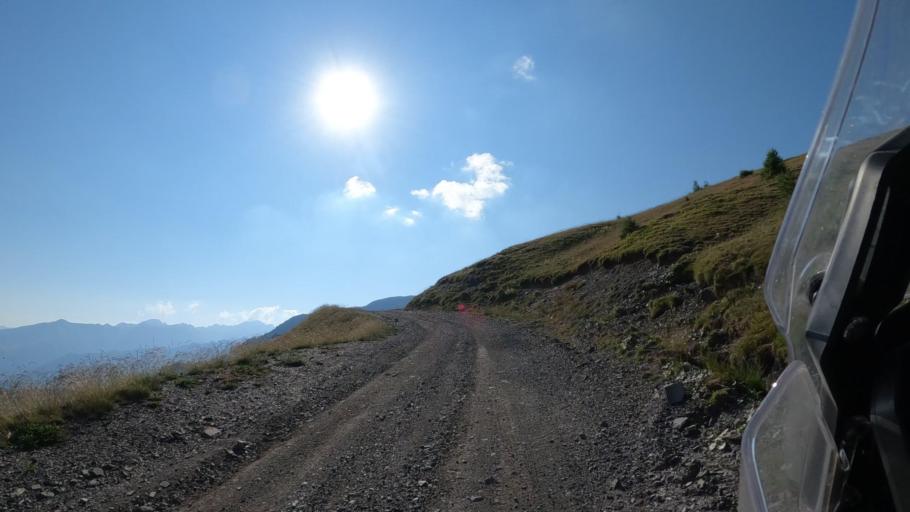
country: FR
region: Provence-Alpes-Cote d'Azur
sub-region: Departement des Hautes-Alpes
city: Guillestre
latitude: 44.6018
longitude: 6.6284
